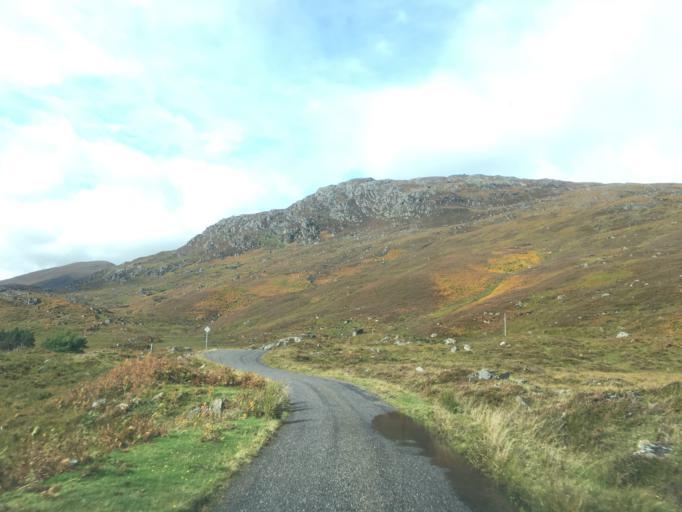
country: GB
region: Scotland
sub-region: Highland
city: Spean Bridge
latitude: 57.3406
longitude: -4.9482
